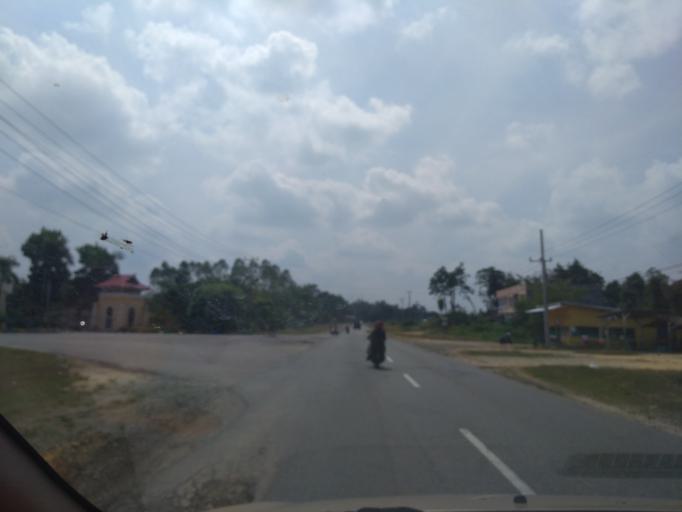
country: ID
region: Jambi
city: Muara Tebo
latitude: -1.4716
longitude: 102.3602
